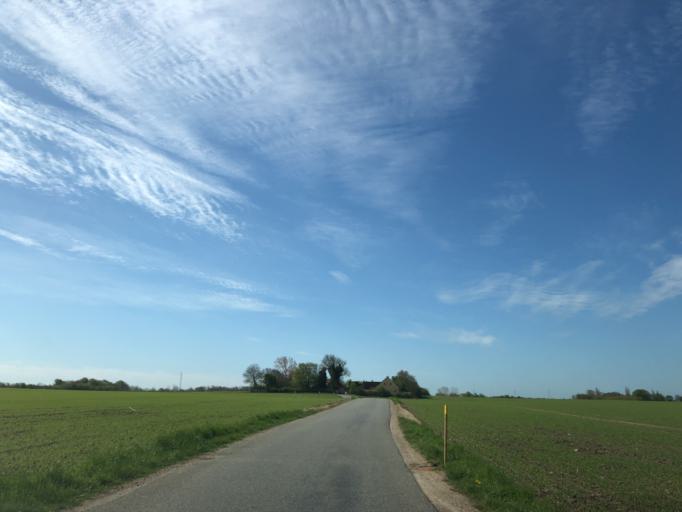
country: DK
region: Zealand
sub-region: Slagelse Kommune
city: Forlev
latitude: 55.3910
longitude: 11.2786
